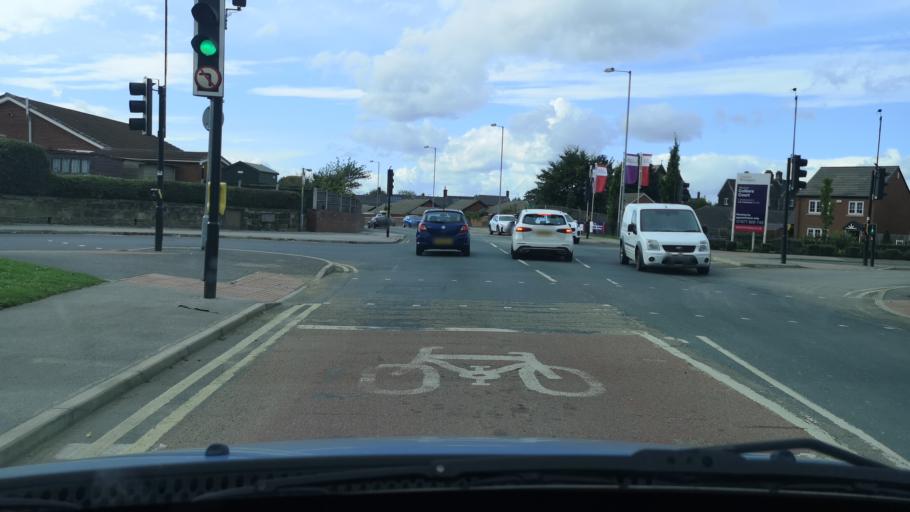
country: GB
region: England
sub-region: City and Borough of Wakefield
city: Featherstone
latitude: 53.6744
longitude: -1.3531
